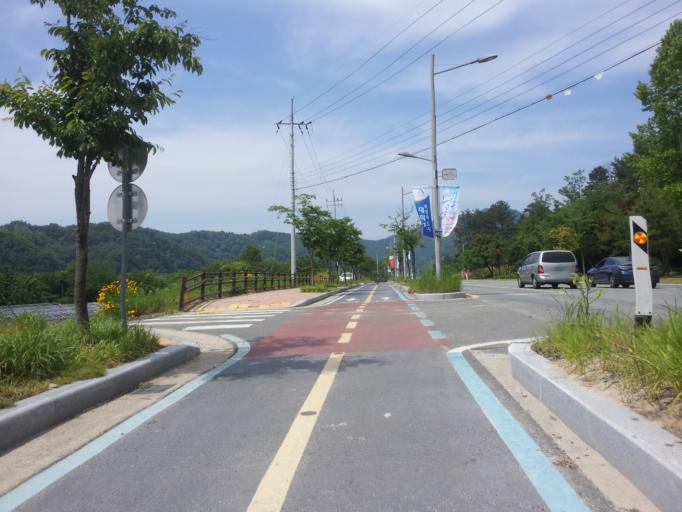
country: KR
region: Daejeon
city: Sintansin
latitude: 36.4603
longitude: 127.4658
